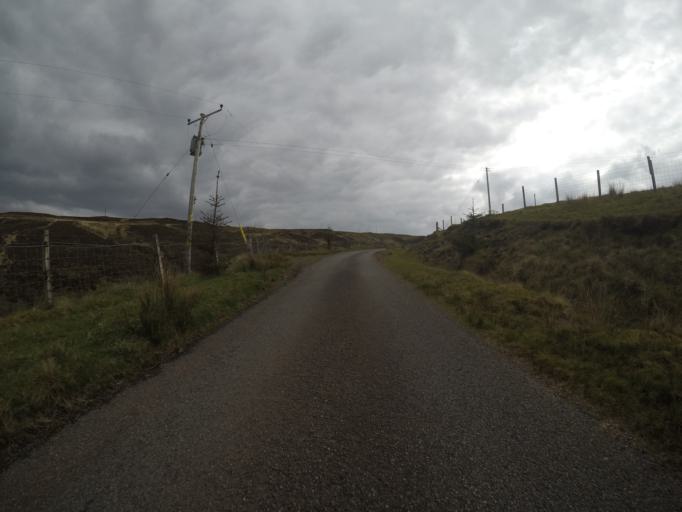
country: GB
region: Scotland
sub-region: Highland
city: Isle of Skye
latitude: 57.2960
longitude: -6.3586
